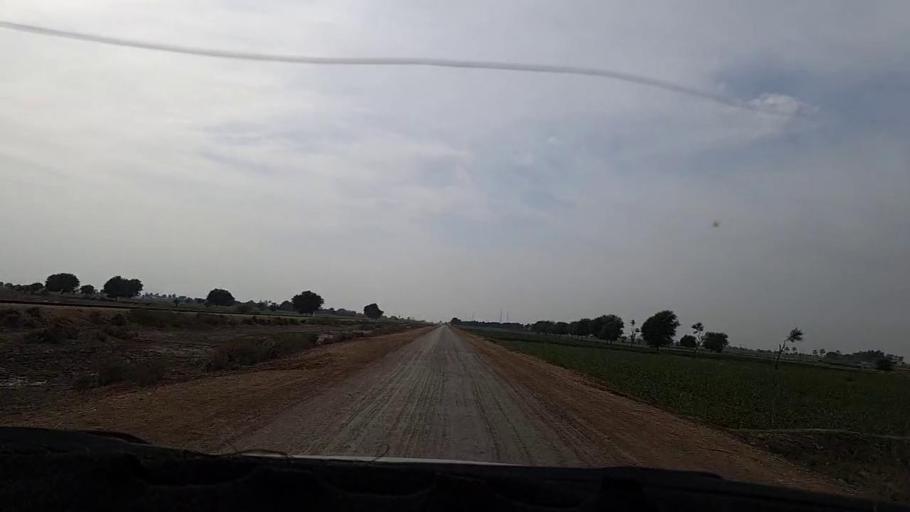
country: PK
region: Sindh
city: Pithoro
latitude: 25.5173
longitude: 69.2572
